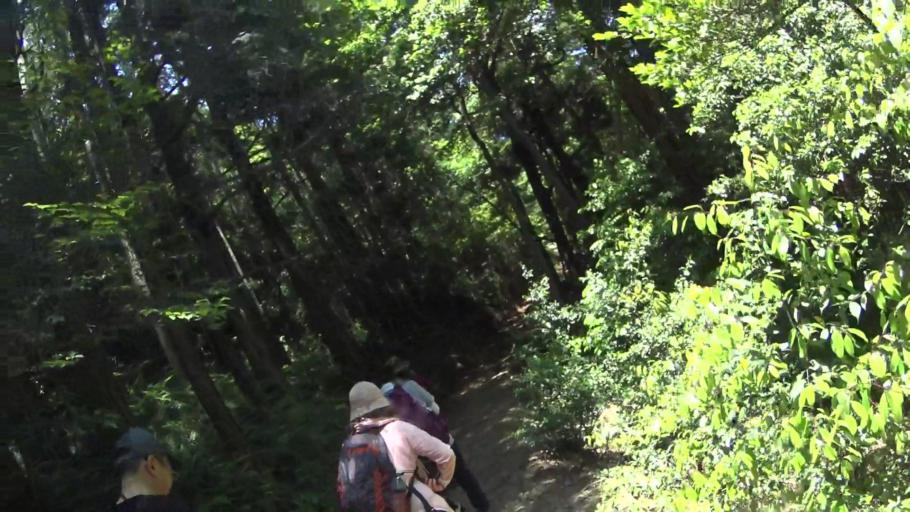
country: JP
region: Kyoto
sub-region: Kyoto-shi
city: Kamigyo-ku
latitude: 35.0130
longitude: 135.8031
